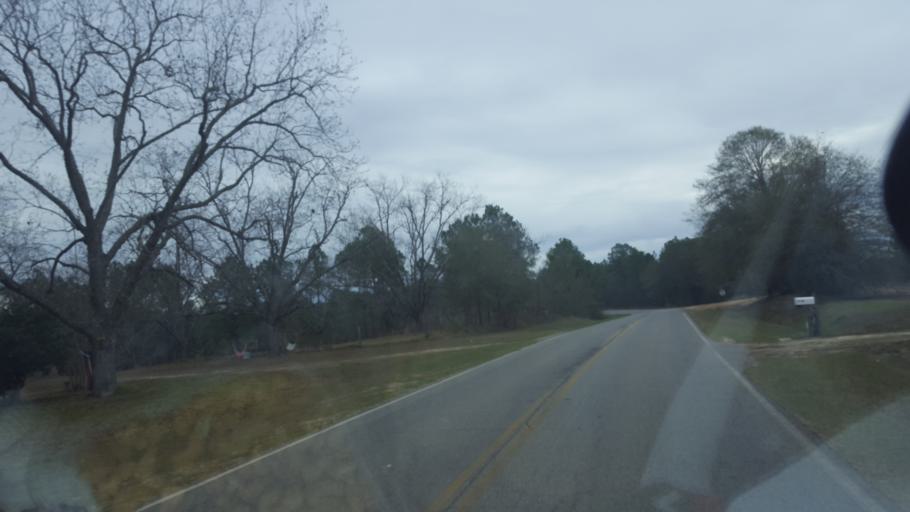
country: US
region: Georgia
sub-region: Ben Hill County
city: Fitzgerald
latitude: 31.7546
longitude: -83.3382
